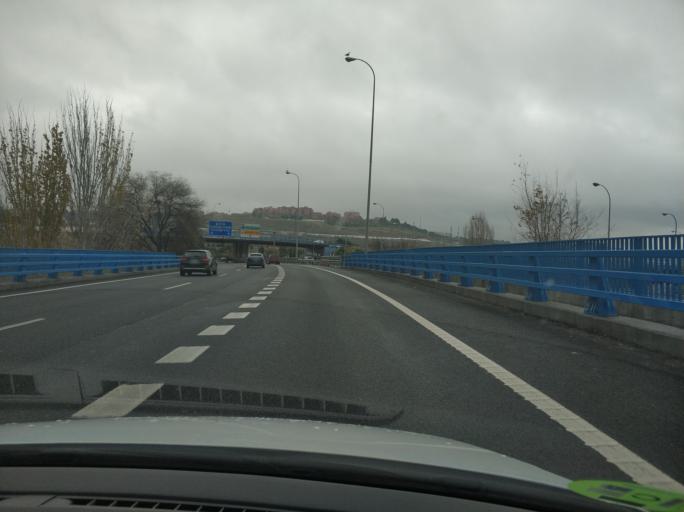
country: ES
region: Madrid
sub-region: Provincia de Madrid
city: Usera
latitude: 40.3816
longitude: -3.6893
